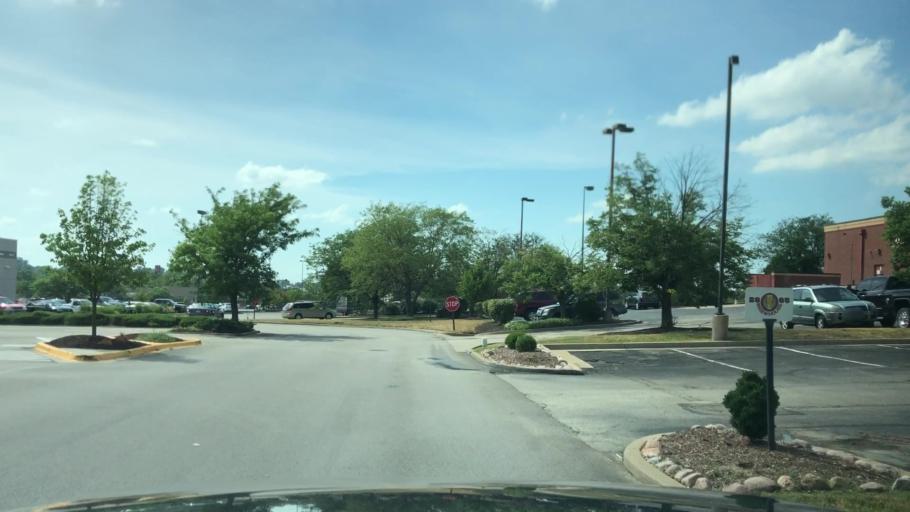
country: US
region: Missouri
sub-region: Saint Charles County
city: Saint Charles
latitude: 38.7829
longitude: -90.5249
